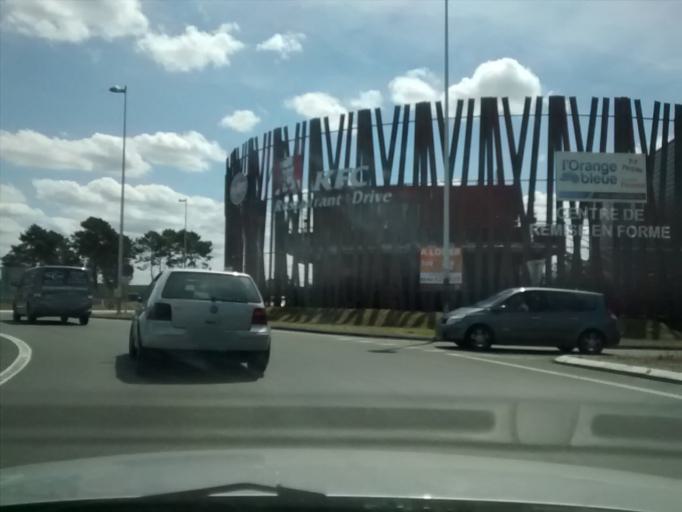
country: FR
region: Pays de la Loire
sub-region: Departement de la Sarthe
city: Ruaudin
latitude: 47.9546
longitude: 0.2274
